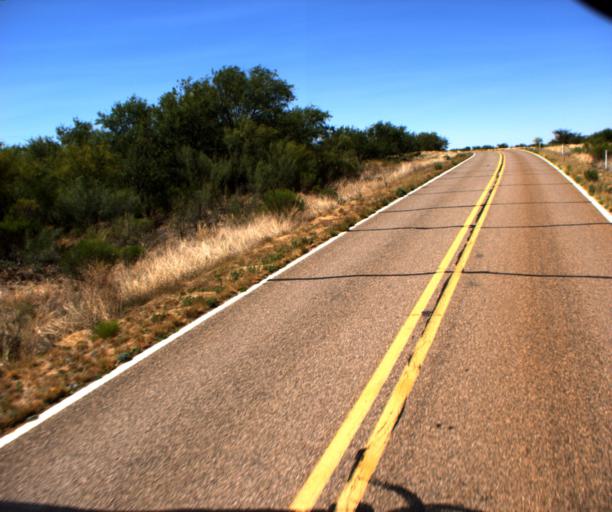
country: US
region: Arizona
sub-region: Pima County
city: Three Points
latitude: 31.6909
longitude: -111.4872
